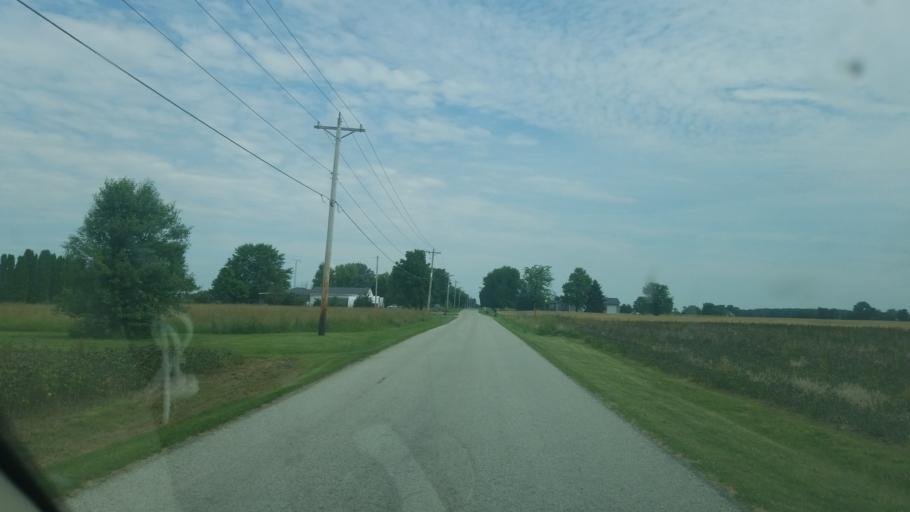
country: US
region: Ohio
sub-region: Seneca County
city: Fostoria
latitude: 41.0636
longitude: -83.4633
